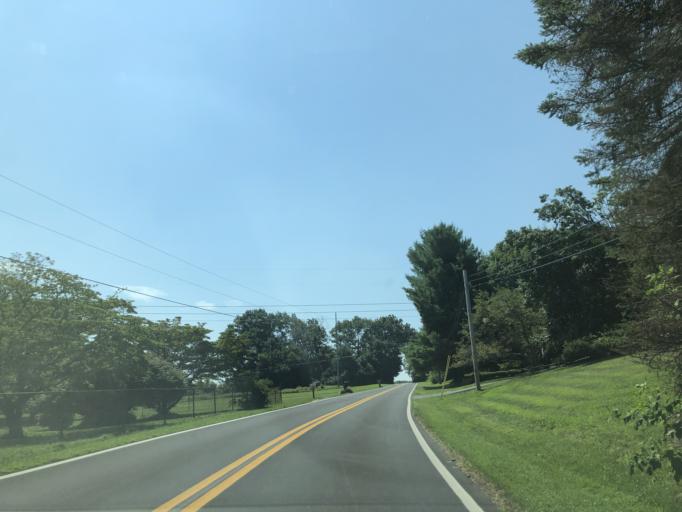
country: US
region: Maryland
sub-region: Carroll County
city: Eldersburg
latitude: 39.4516
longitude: -76.9708
